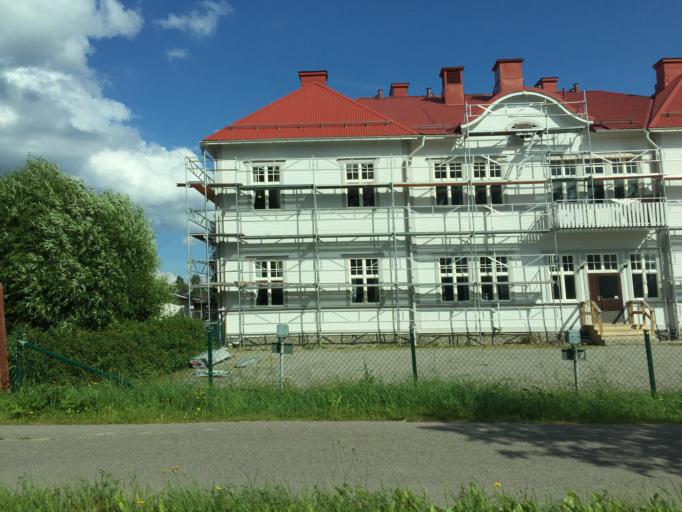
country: SE
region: Gaevleborg
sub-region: Bollnas Kommun
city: Arbra
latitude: 61.5188
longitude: 16.3632
